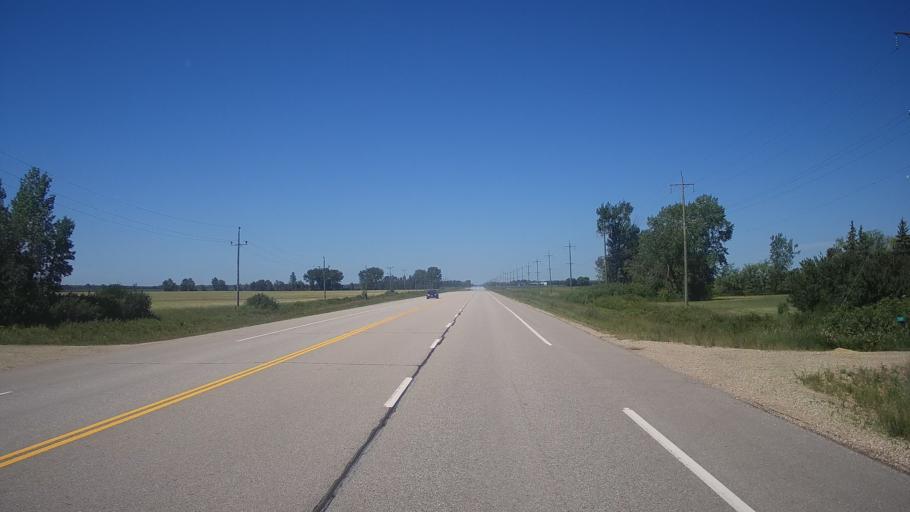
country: CA
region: Manitoba
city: Neepawa
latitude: 50.2250
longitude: -99.2830
